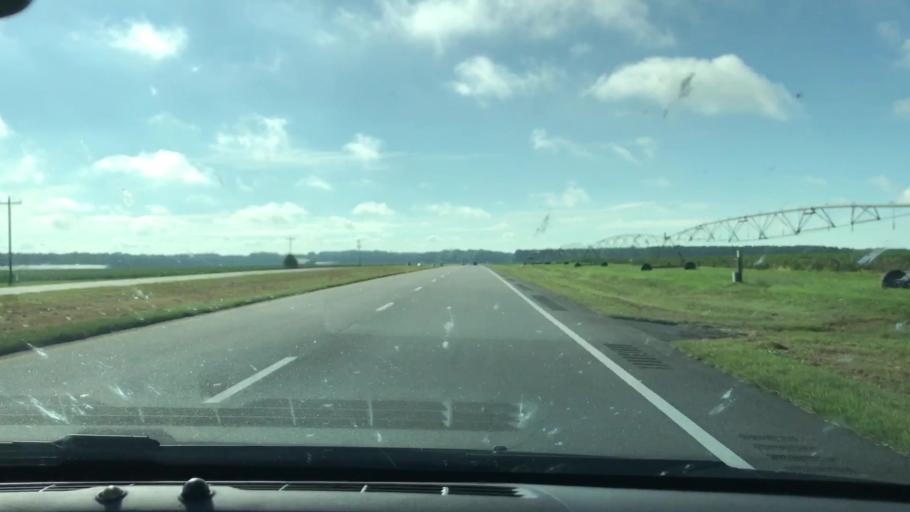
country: US
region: Georgia
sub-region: Terrell County
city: Dawson
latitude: 31.7026
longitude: -84.3283
